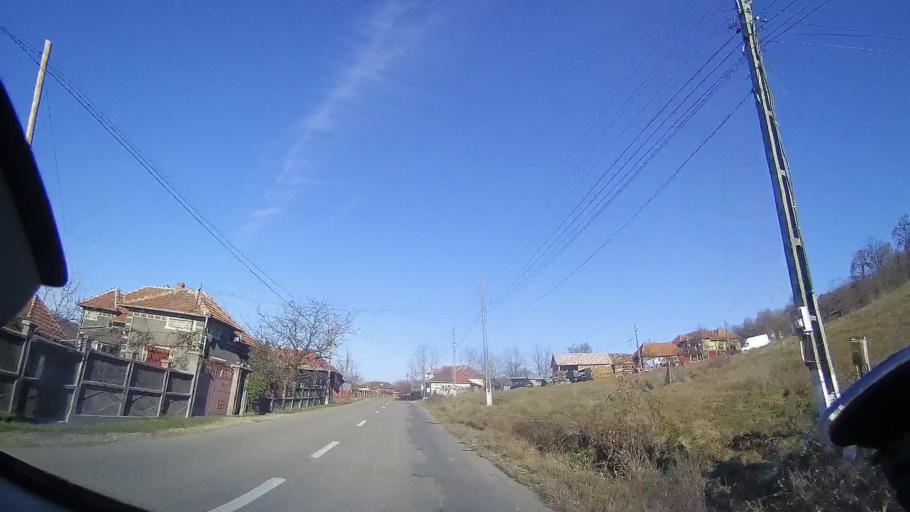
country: RO
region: Bihor
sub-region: Comuna Bratca
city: Bratca
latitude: 46.9336
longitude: 22.6031
